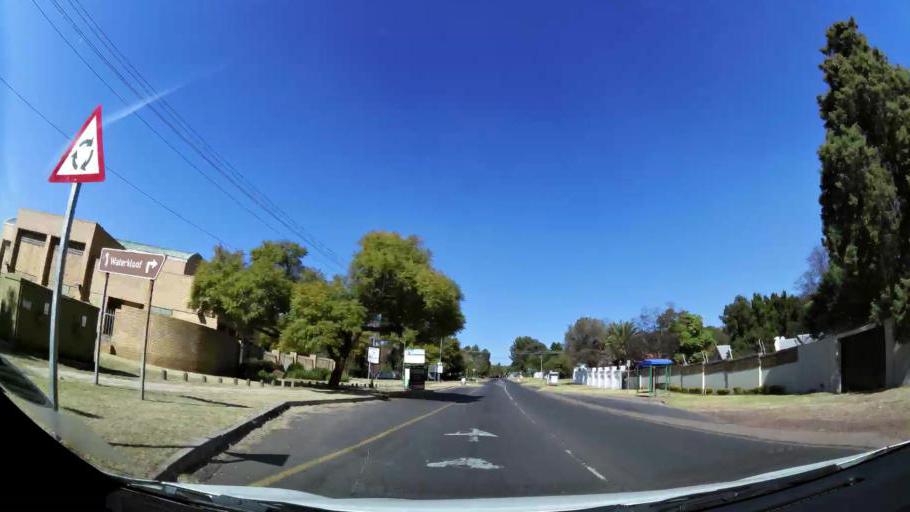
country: ZA
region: Gauteng
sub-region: City of Tshwane Metropolitan Municipality
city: Pretoria
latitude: -25.7890
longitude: 28.2390
